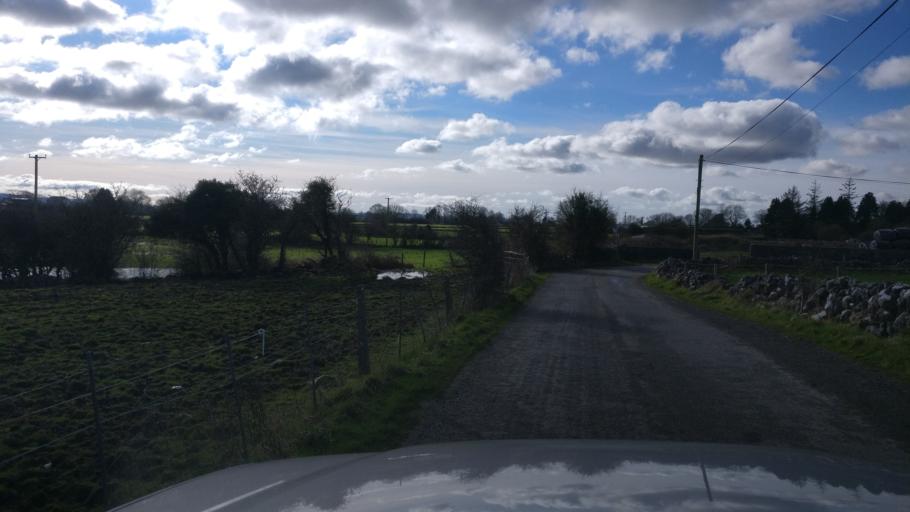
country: IE
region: Connaught
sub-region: County Galway
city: Oranmore
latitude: 53.2846
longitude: -8.8882
